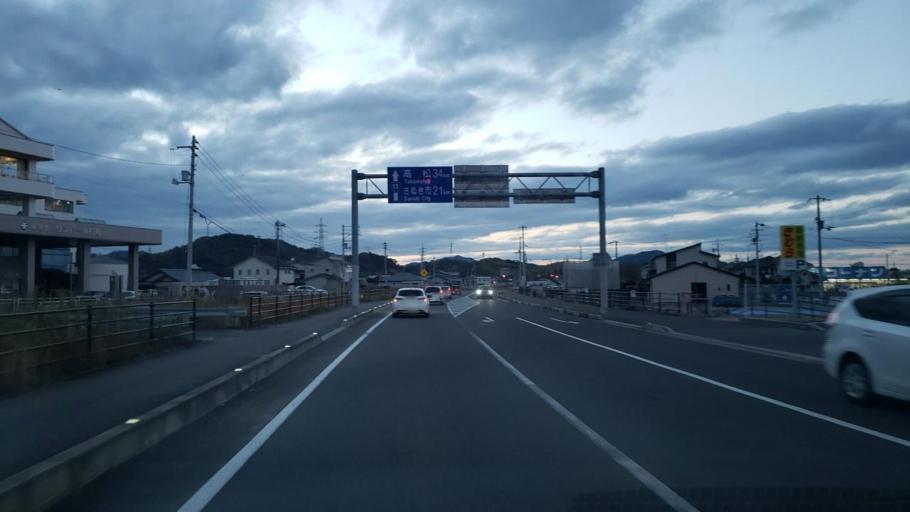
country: JP
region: Tokushima
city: Kamojimacho-jogejima
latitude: 34.2400
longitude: 134.3531
